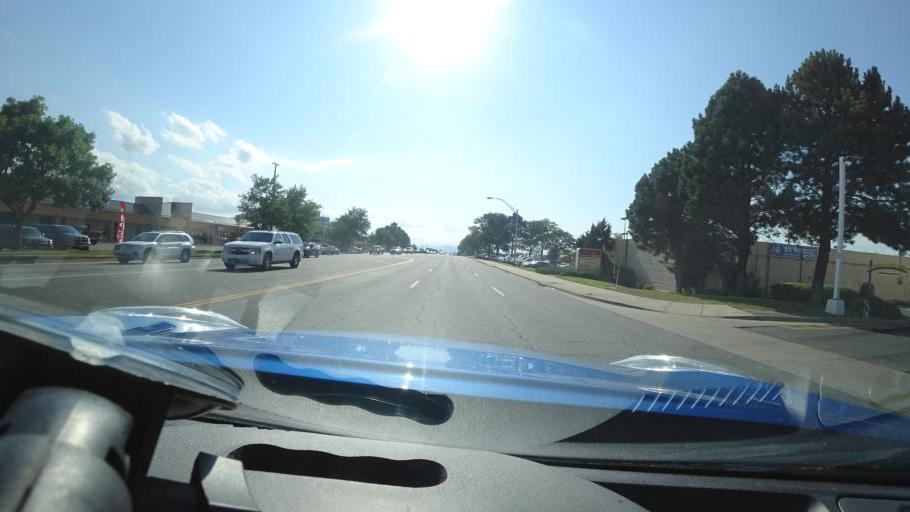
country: US
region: Colorado
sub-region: Adams County
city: Aurora
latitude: 39.6748
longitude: -104.8665
